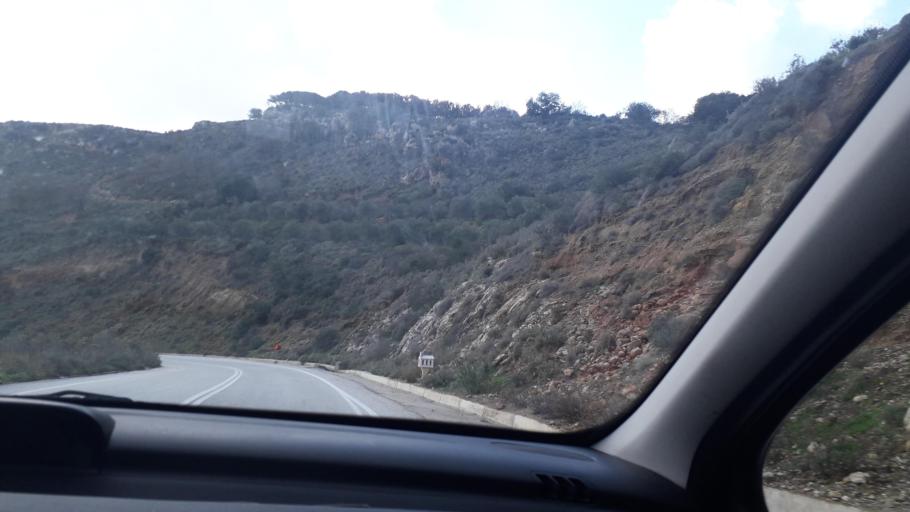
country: GR
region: Crete
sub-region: Nomos Rethymnis
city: Rethymno
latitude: 35.3102
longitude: 24.5350
